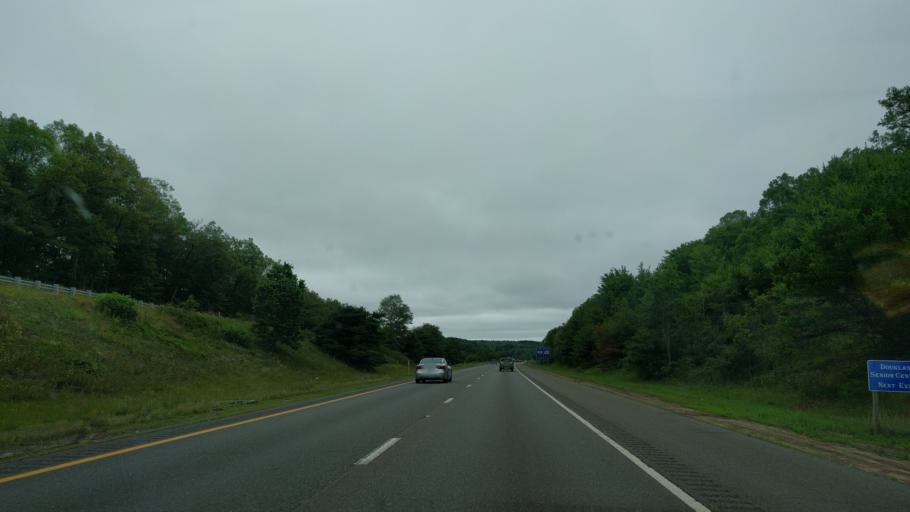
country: US
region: Massachusetts
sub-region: Worcester County
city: East Douglas
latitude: 42.0949
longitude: -71.7000
